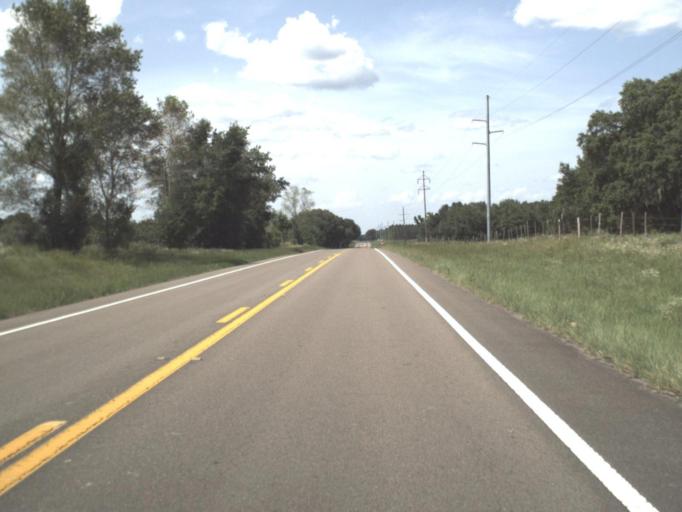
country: US
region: Florida
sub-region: Gilchrist County
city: Trenton
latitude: 29.7164
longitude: -82.7512
